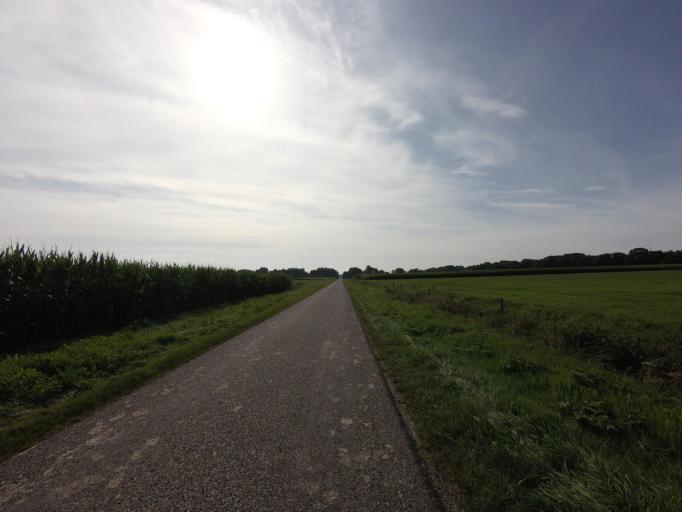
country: NL
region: Drenthe
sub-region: Gemeente Aa en Hunze
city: Anloo
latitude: 52.9432
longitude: 6.6746
